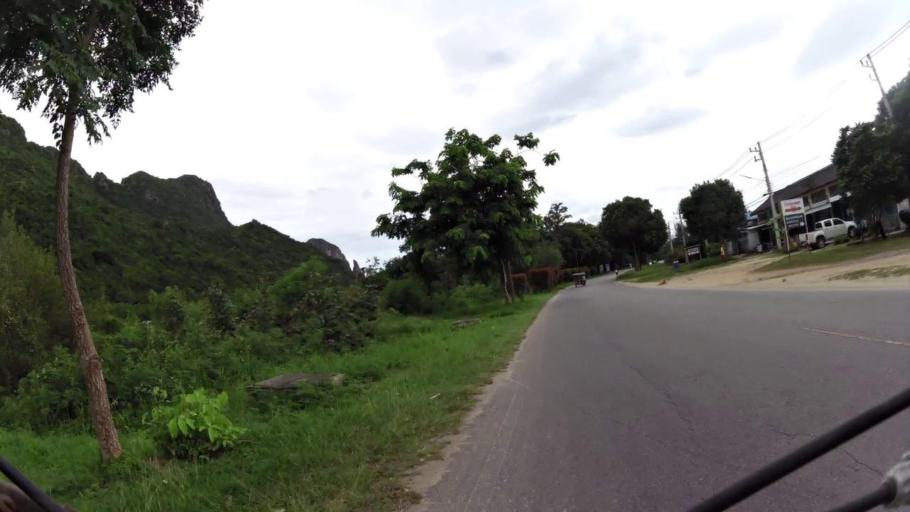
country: TH
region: Prachuap Khiri Khan
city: Prachuap Khiri Khan
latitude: 11.7563
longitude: 99.7931
